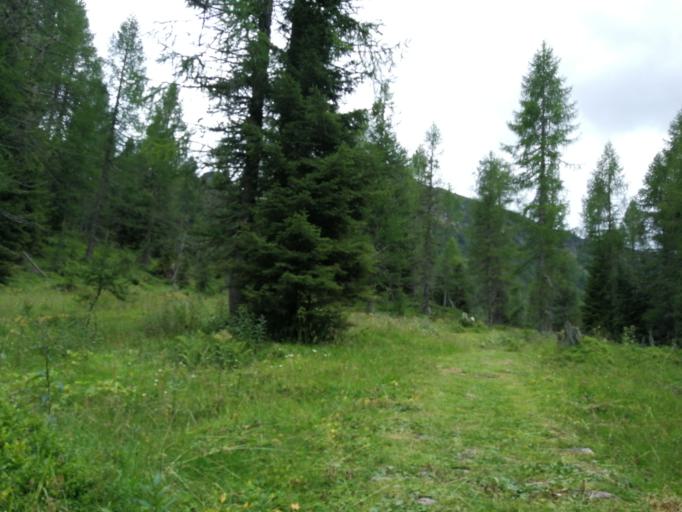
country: IT
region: Trentino-Alto Adige
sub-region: Provincia di Trento
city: Brione
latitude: 45.9340
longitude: 10.5350
